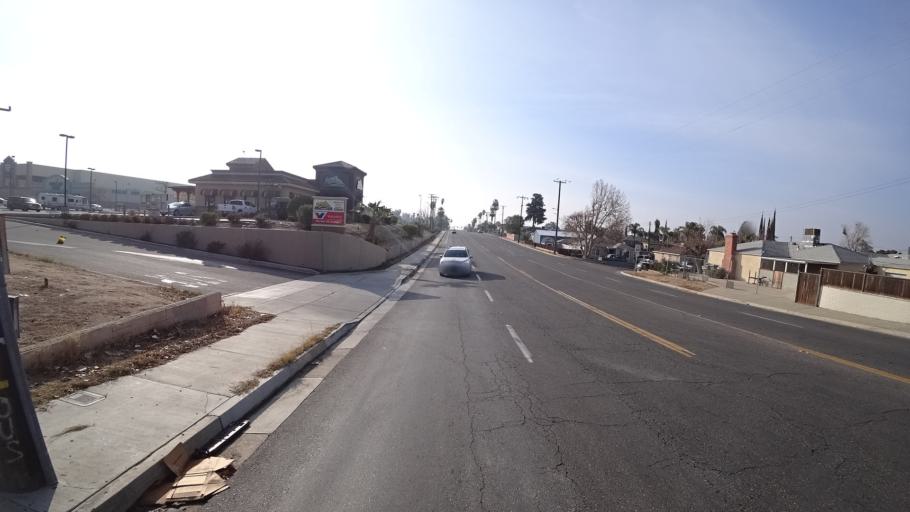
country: US
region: California
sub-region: Kern County
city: Bakersfield
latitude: 35.3971
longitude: -118.9762
